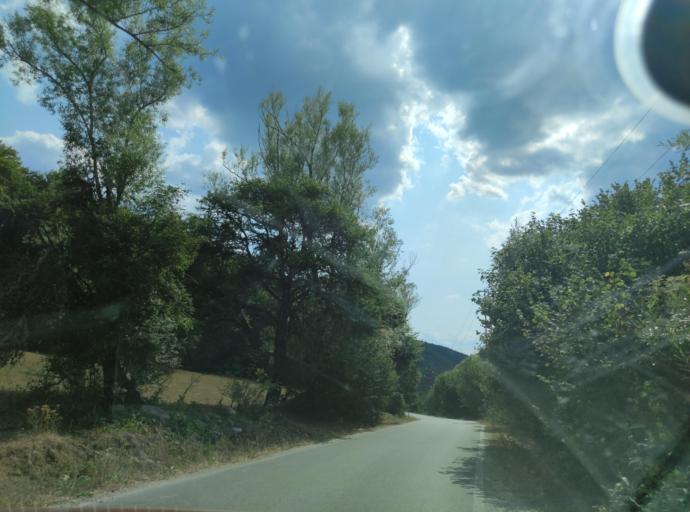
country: BG
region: Blagoevgrad
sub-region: Obshtina Belitsa
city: Belitsa
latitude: 42.0145
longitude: 23.5698
